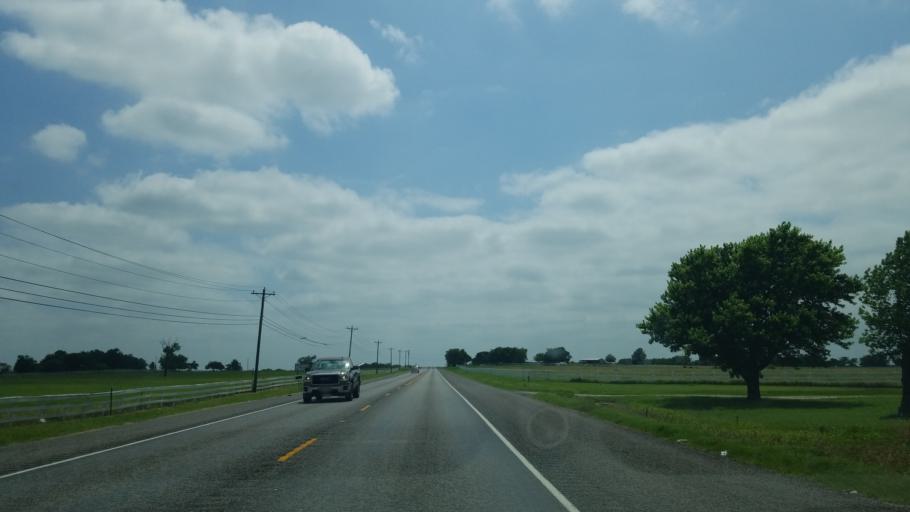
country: US
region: Texas
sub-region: Denton County
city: Krugerville
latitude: 33.3027
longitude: -97.0673
